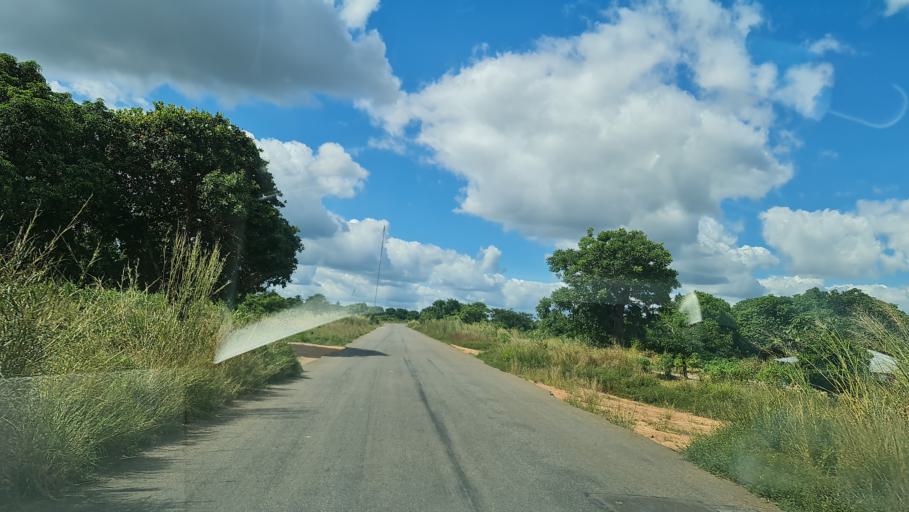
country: MZ
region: Zambezia
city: Quelimane
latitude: -17.5075
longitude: 36.2405
